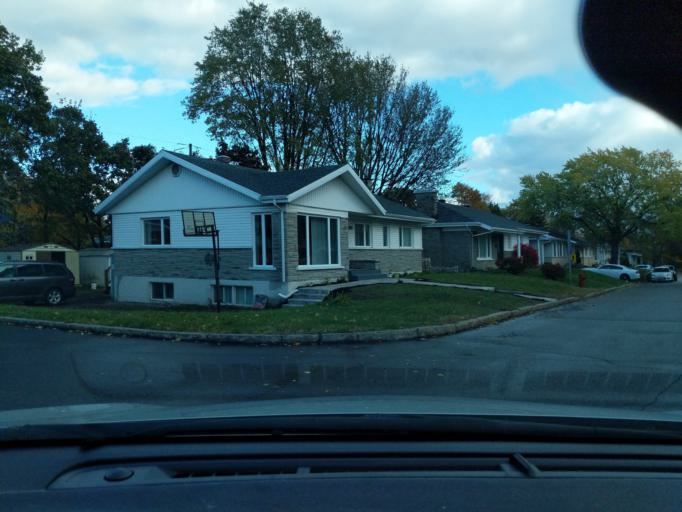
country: CA
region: Quebec
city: L'Ancienne-Lorette
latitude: 46.7619
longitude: -71.2907
